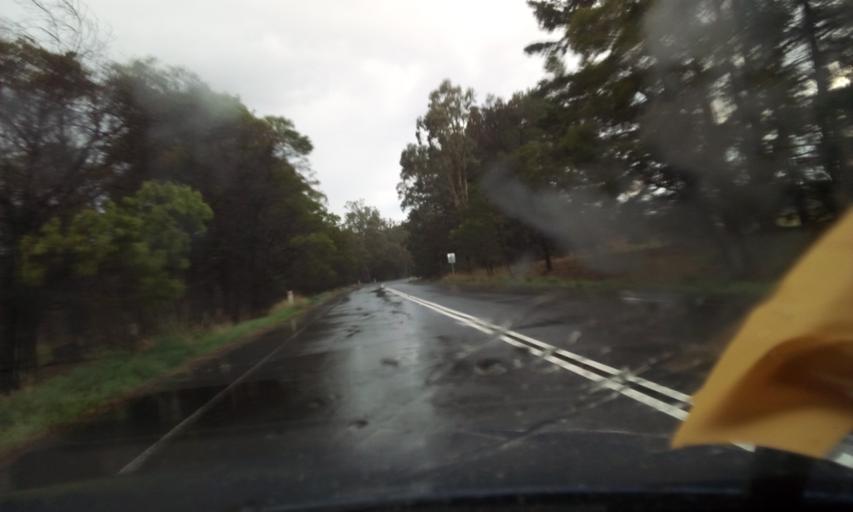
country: AU
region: New South Wales
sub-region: Wollondilly
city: Douglas Park
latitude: -34.2619
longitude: 150.7200
